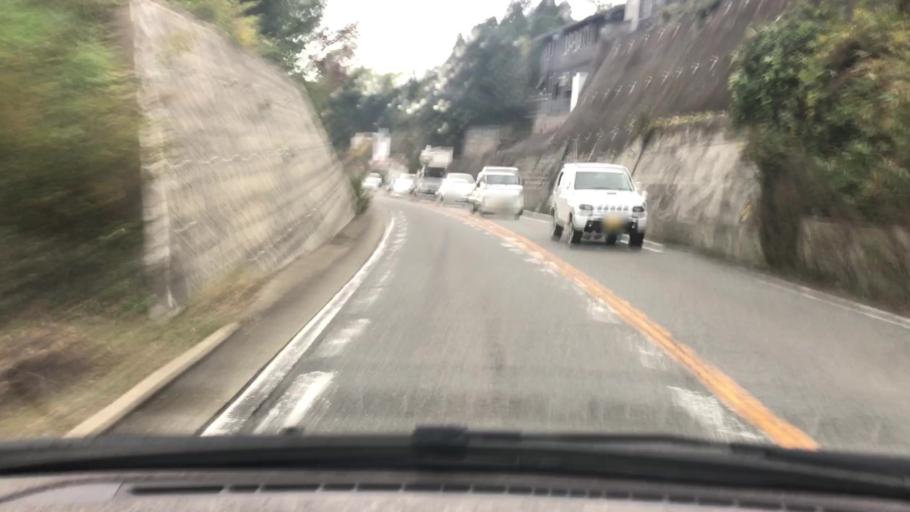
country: JP
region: Hyogo
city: Sandacho
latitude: 34.8345
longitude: 135.2713
